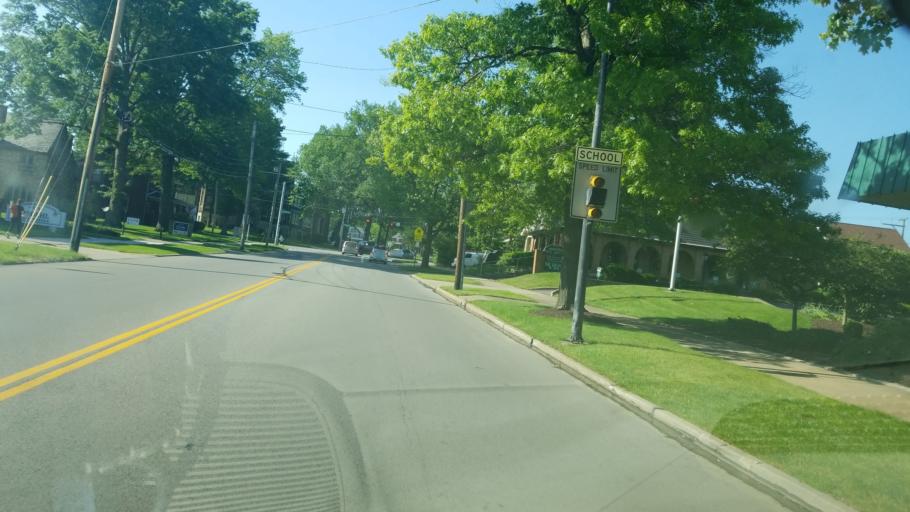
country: US
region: Ohio
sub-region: Wayne County
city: Wooster
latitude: 40.8037
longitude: -81.9414
